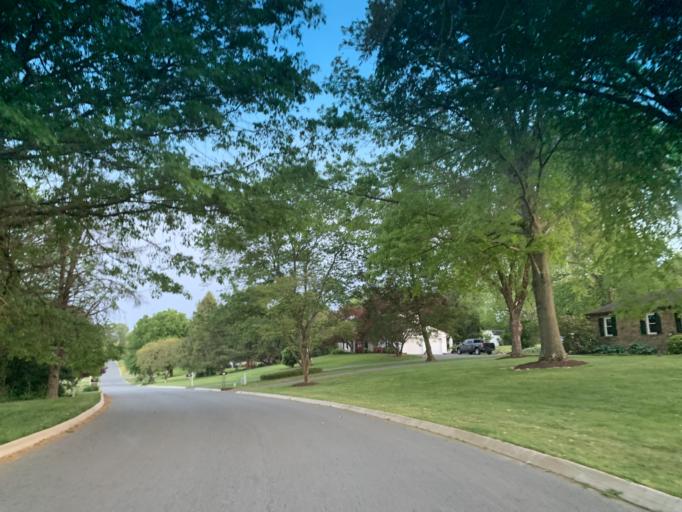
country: US
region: Maryland
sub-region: Harford County
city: South Bel Air
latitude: 39.5896
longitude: -76.2808
